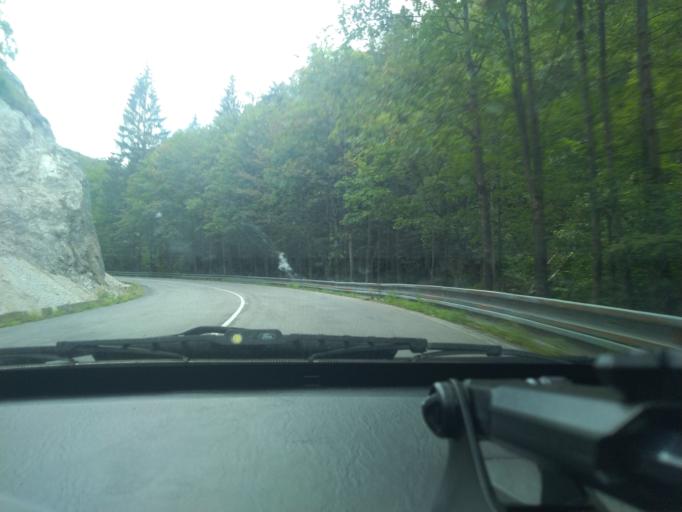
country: SK
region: Banskobystricky
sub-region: Okres Banska Bystrica
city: Banska Bystrica
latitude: 48.8222
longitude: 19.0229
